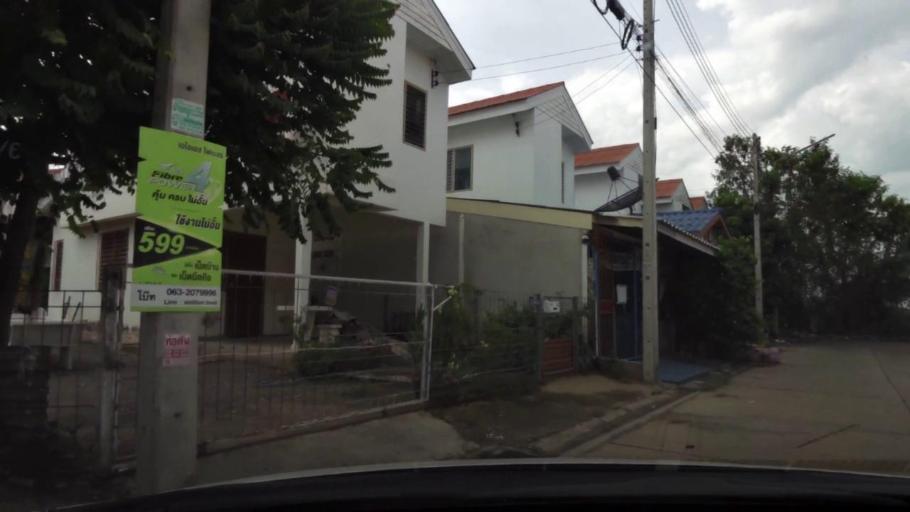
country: TH
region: Ratchaburi
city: Ratchaburi
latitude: 13.5390
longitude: 99.7926
